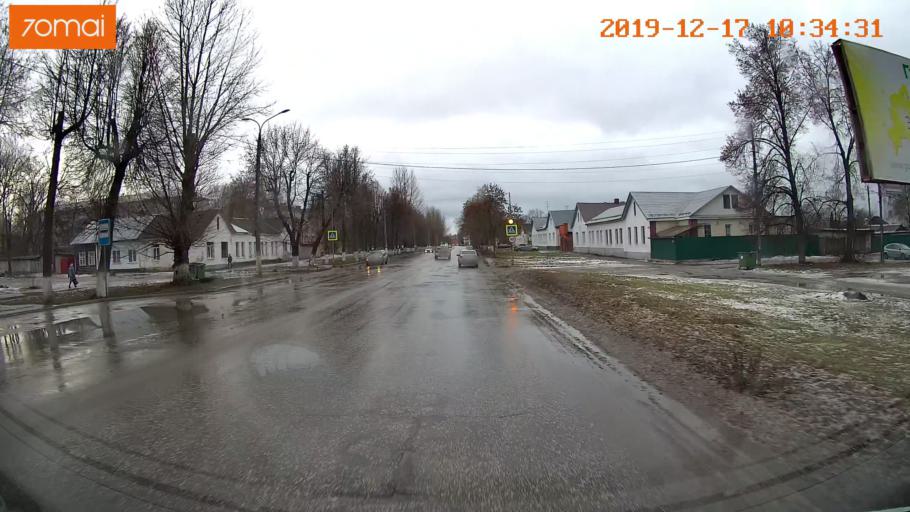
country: RU
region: Vladimir
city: Gus'-Khrustal'nyy
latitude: 55.6181
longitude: 40.6749
